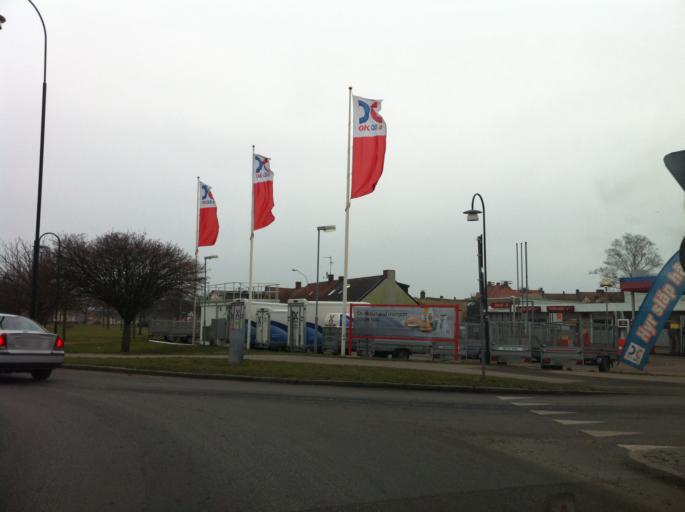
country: SE
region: Skane
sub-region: Landskrona
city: Landskrona
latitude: 55.8726
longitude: 12.8498
